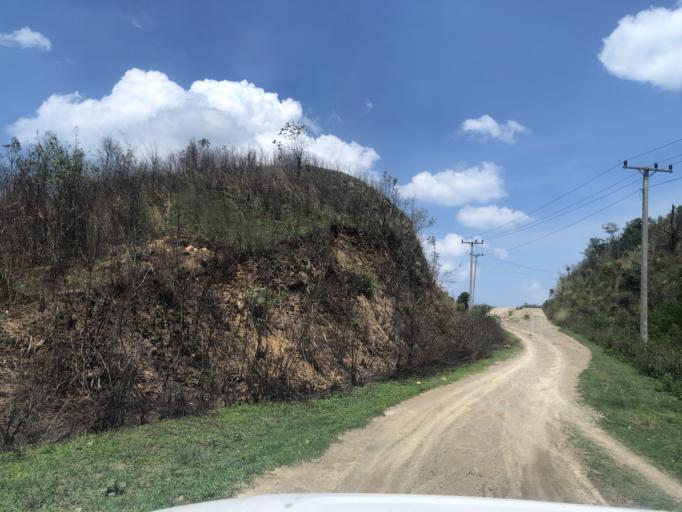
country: LA
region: Phongsali
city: Phongsali
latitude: 21.4222
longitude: 102.1791
